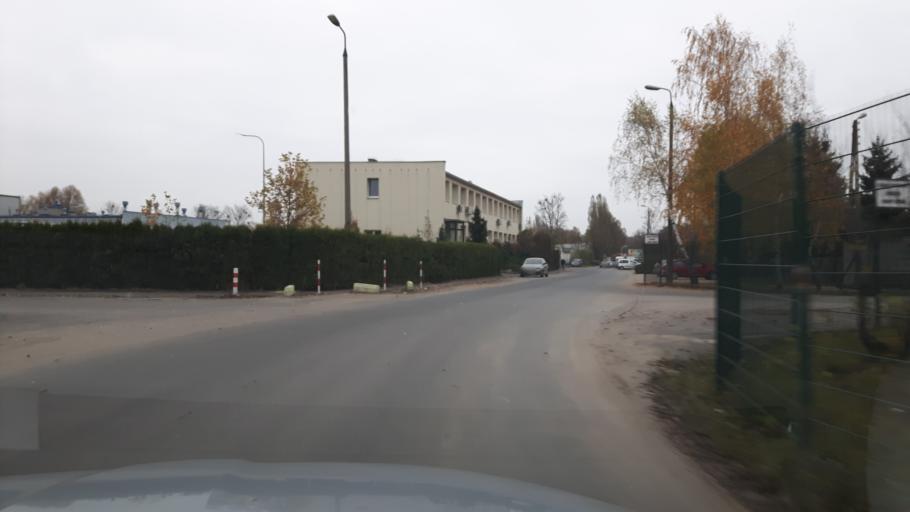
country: PL
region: Masovian Voivodeship
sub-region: Warszawa
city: Praga Polnoc
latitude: 52.2720
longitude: 21.0283
